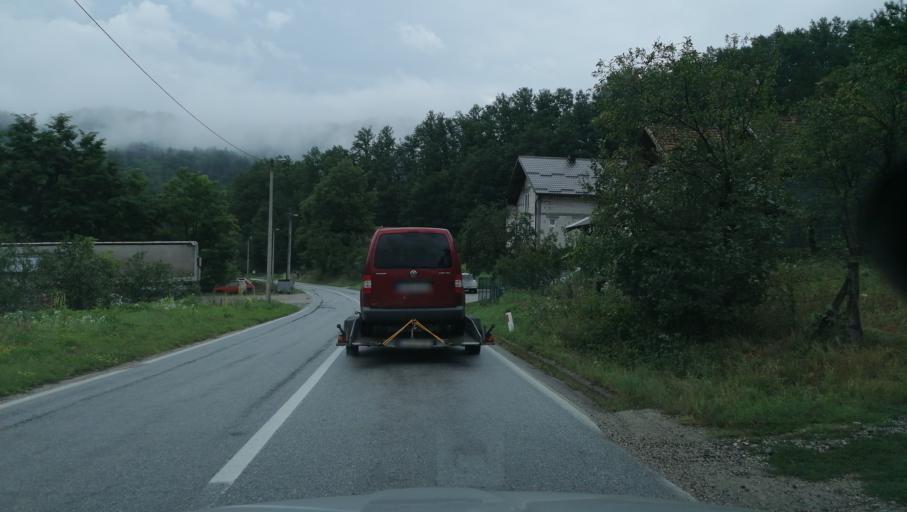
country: BA
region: Republika Srpska
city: Visegrad
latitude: 43.7805
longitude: 19.3608
